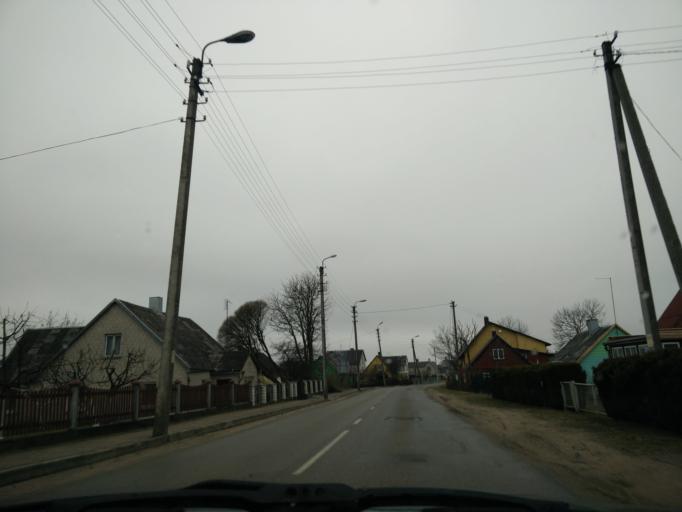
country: LT
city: Raseiniai
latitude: 55.3804
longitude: 23.1089
